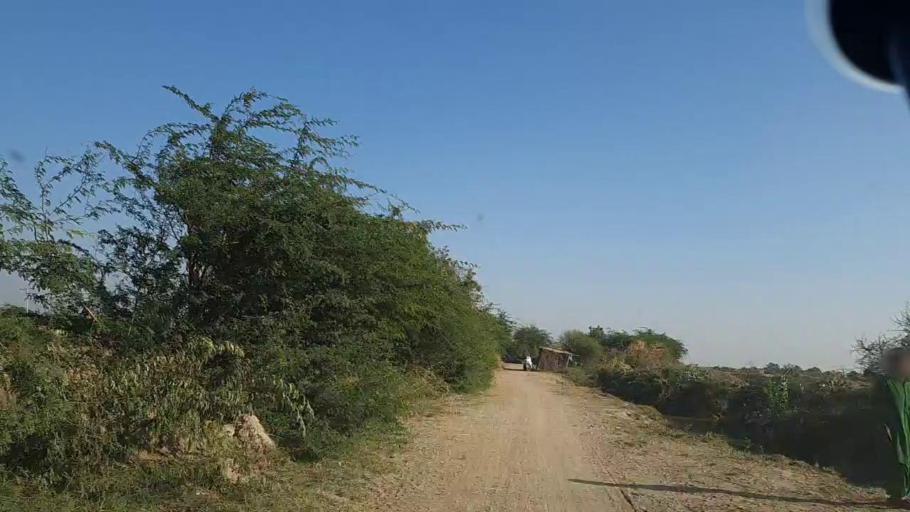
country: PK
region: Sindh
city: Chuhar Jamali
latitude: 24.5684
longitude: 68.0459
